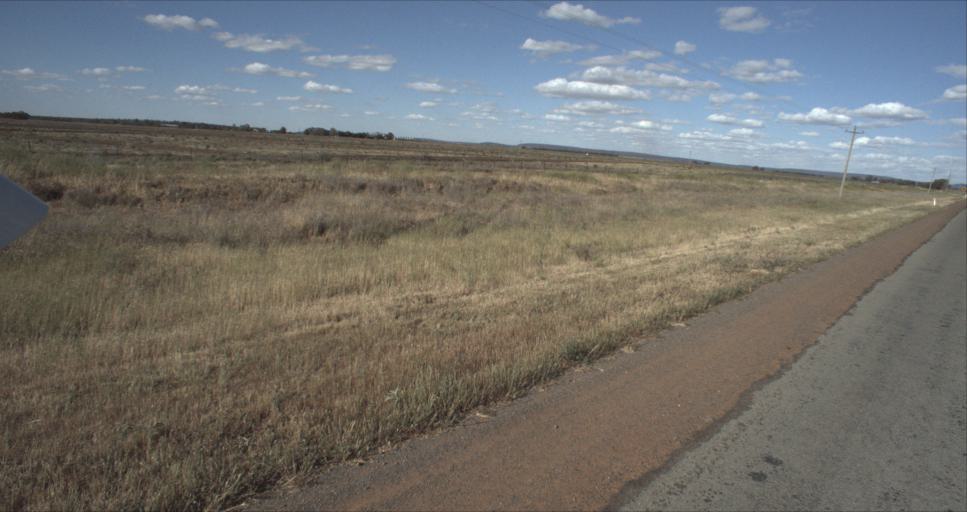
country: AU
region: New South Wales
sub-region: Leeton
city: Leeton
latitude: -34.4571
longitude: 146.2910
